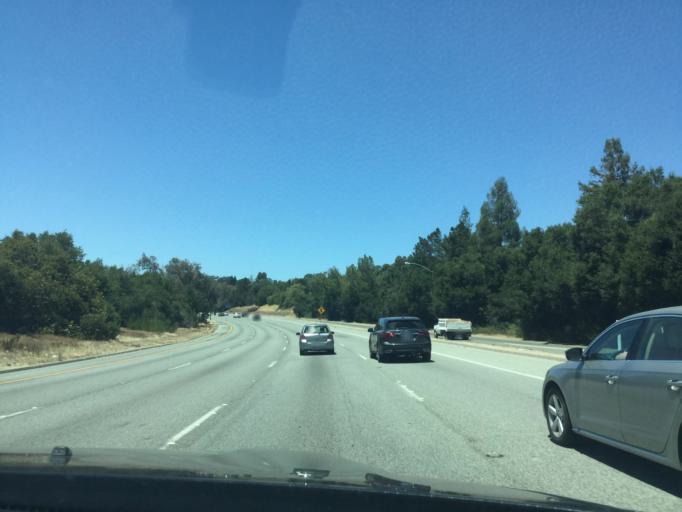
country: US
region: California
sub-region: Santa Clara County
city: Loyola
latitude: 37.3627
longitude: -122.1211
